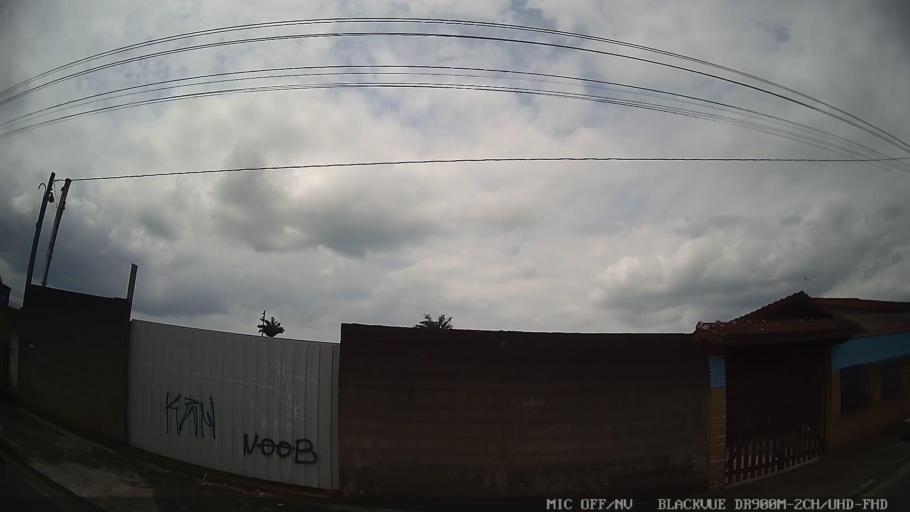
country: BR
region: Sao Paulo
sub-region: Caraguatatuba
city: Caraguatatuba
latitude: -23.6748
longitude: -45.4451
